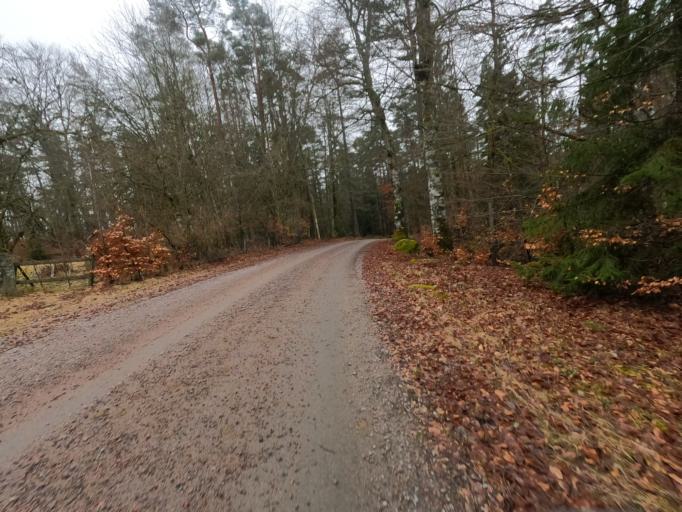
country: SE
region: Kronoberg
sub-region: Markaryds Kommun
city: Stromsnasbruk
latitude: 56.8205
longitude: 13.5603
